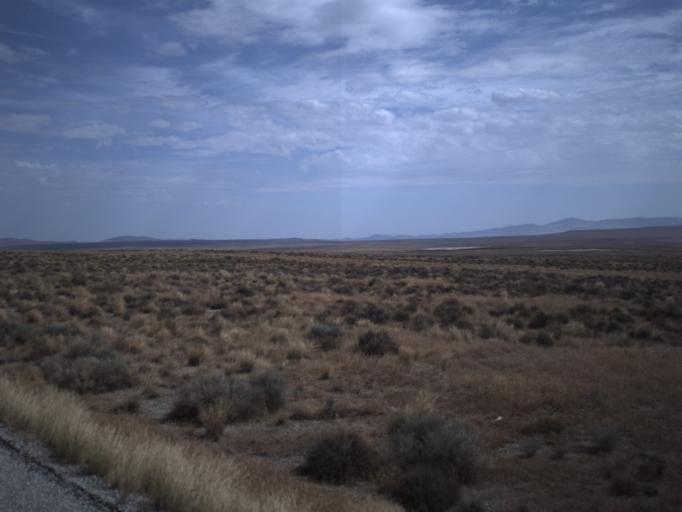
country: US
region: Utah
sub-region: Tooele County
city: Wendover
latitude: 41.4888
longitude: -113.6208
